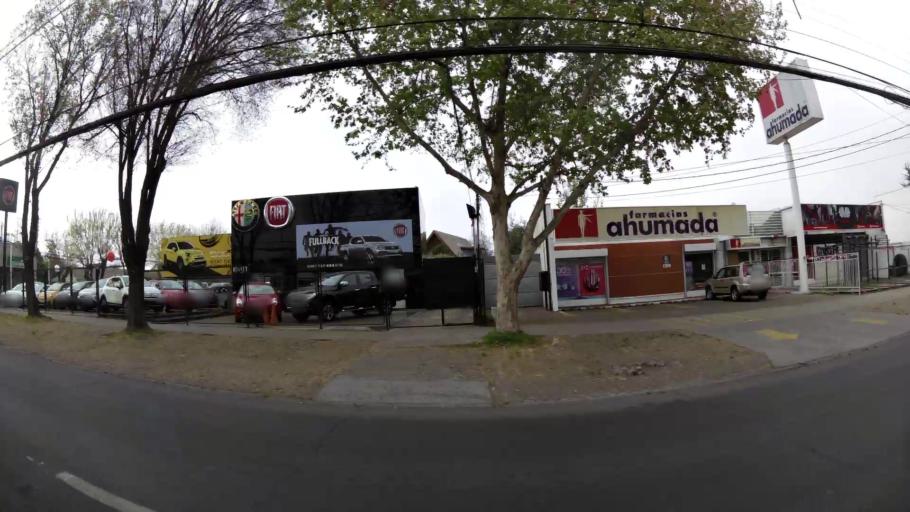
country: CL
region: Santiago Metropolitan
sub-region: Provincia de Santiago
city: Villa Presidente Frei, Nunoa, Santiago, Chile
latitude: -33.3852
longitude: -70.5550
